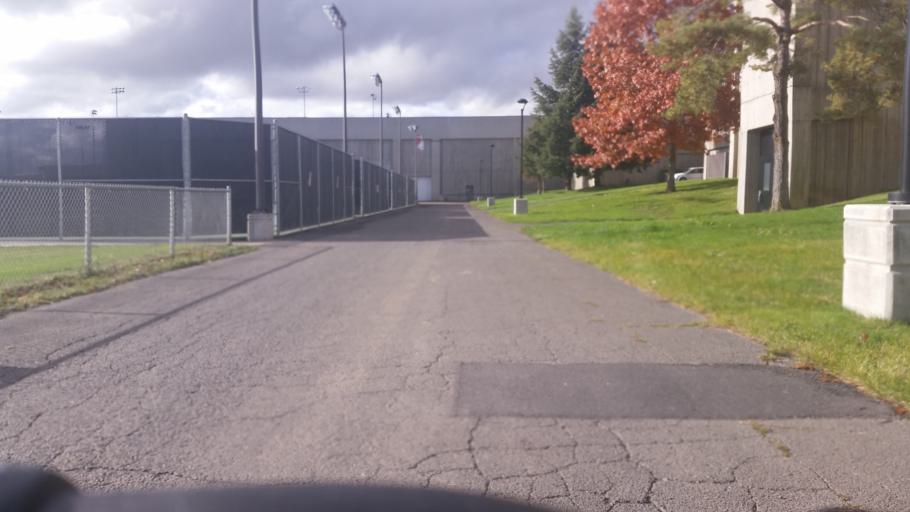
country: US
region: Washington
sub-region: Spokane County
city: Cheney
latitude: 47.4903
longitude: -117.5877
